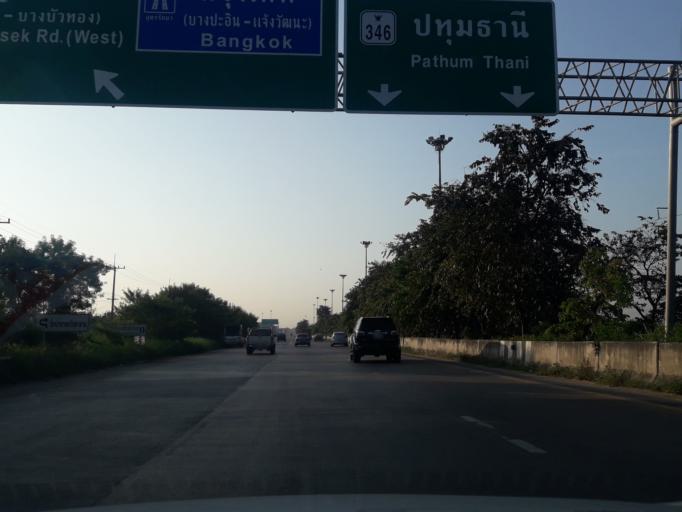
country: TH
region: Phra Nakhon Si Ayutthaya
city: Bang Pa-in
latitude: 14.1645
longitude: 100.5647
